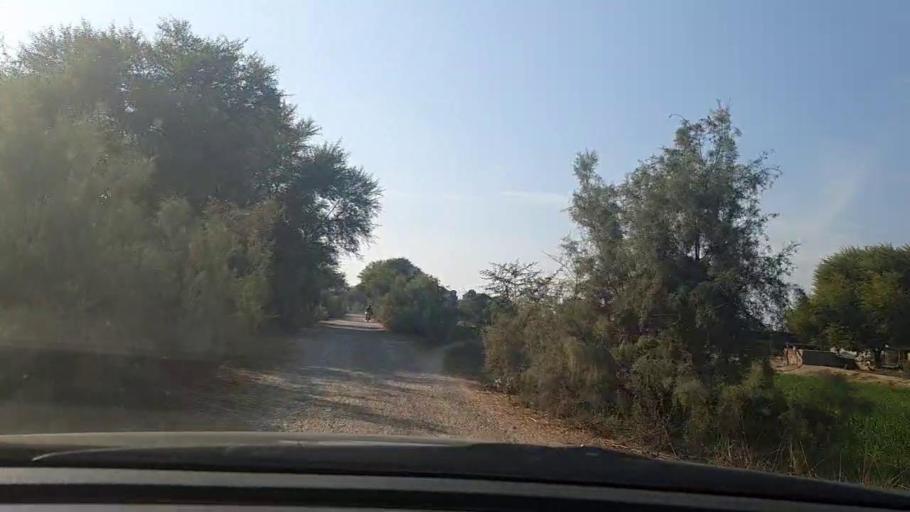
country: PK
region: Sindh
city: Sehwan
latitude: 26.3046
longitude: 68.0003
